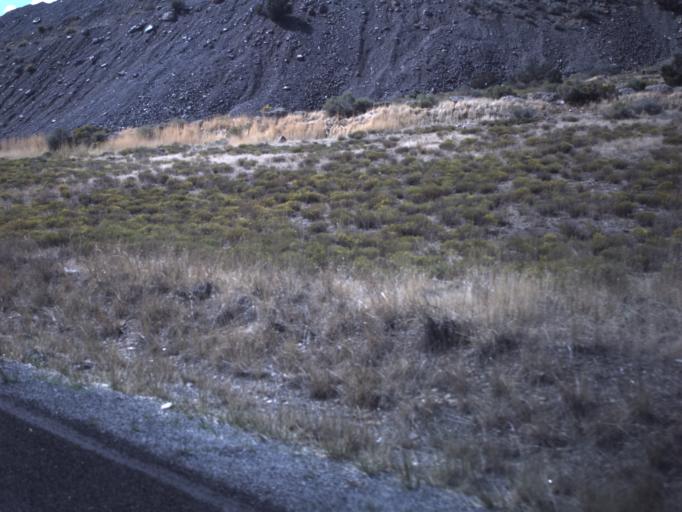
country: US
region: Utah
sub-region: Utah County
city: Santaquin
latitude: 40.0116
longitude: -111.8011
